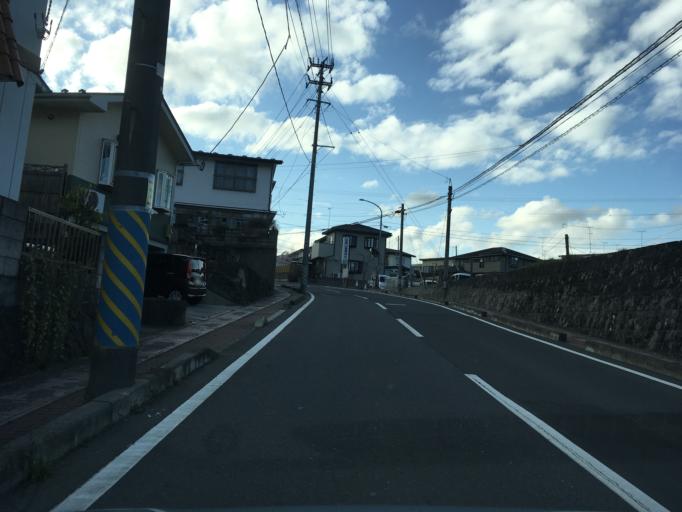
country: JP
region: Miyagi
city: Ishinomaki
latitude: 38.4303
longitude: 141.3017
